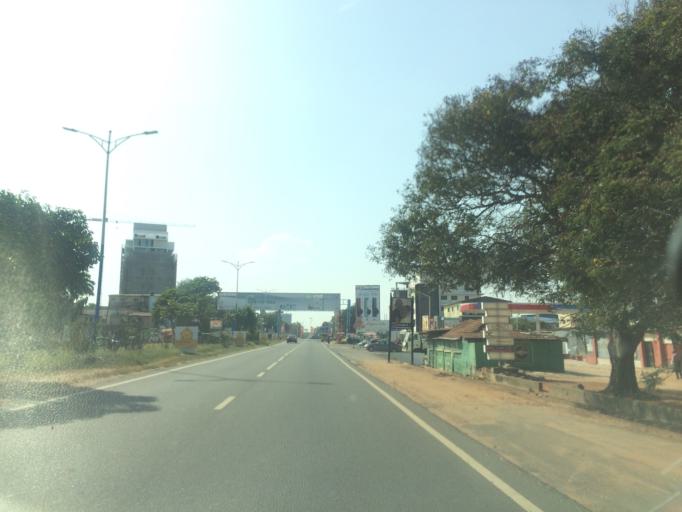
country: GH
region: Greater Accra
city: Accra
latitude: 5.5656
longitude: -0.1784
